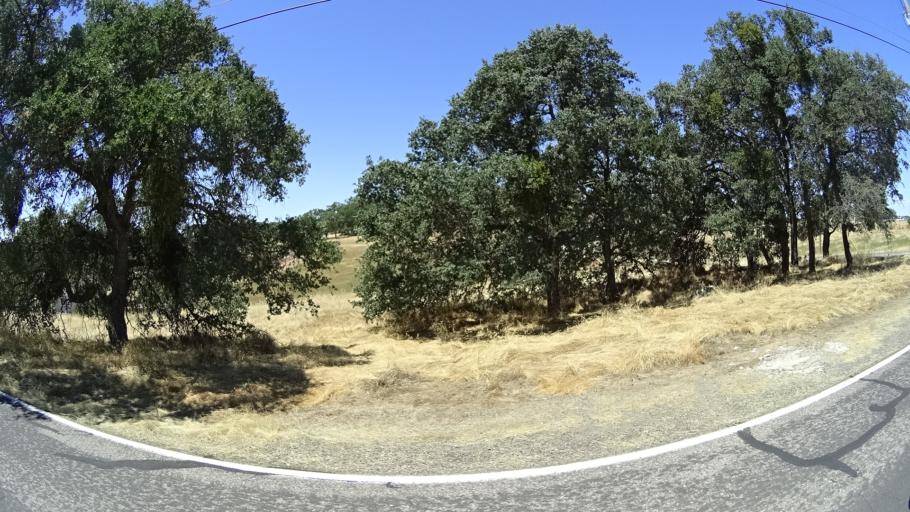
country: US
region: California
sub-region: Calaveras County
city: Rancho Calaveras
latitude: 38.1503
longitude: -120.8435
